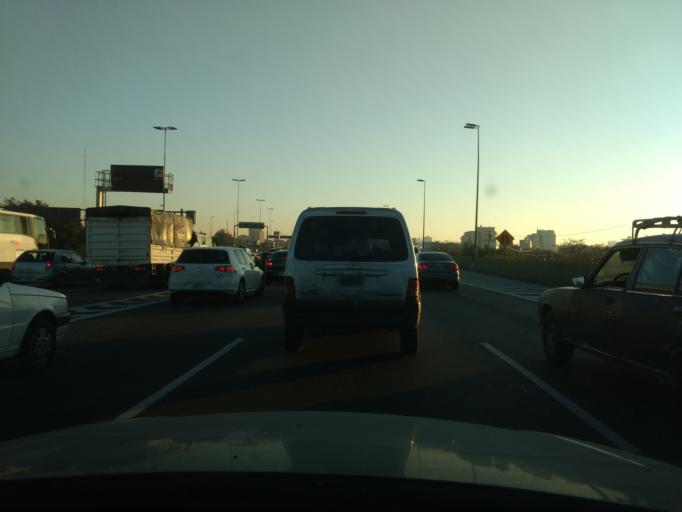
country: AR
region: Buenos Aires F.D.
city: Villa Lugano
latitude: -34.6463
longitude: -58.4628
